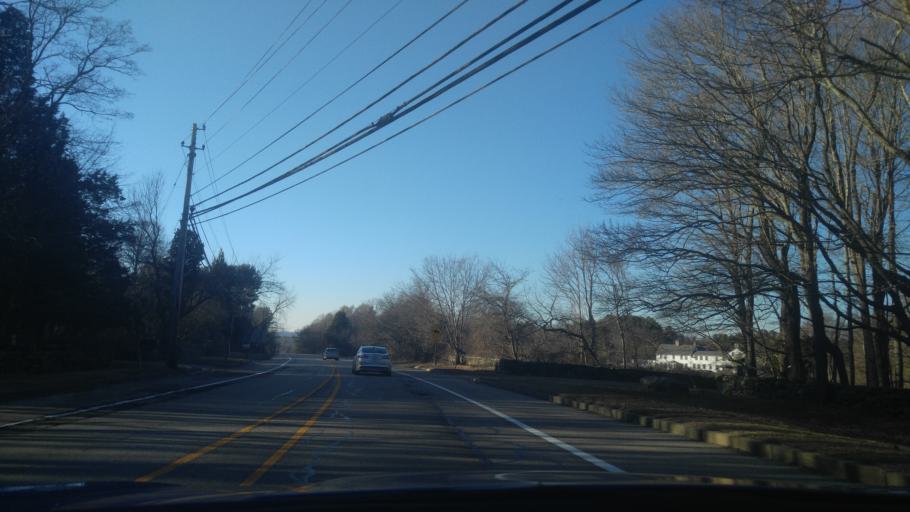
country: US
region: Rhode Island
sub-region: Washington County
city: North Kingstown
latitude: 41.5316
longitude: -71.4290
